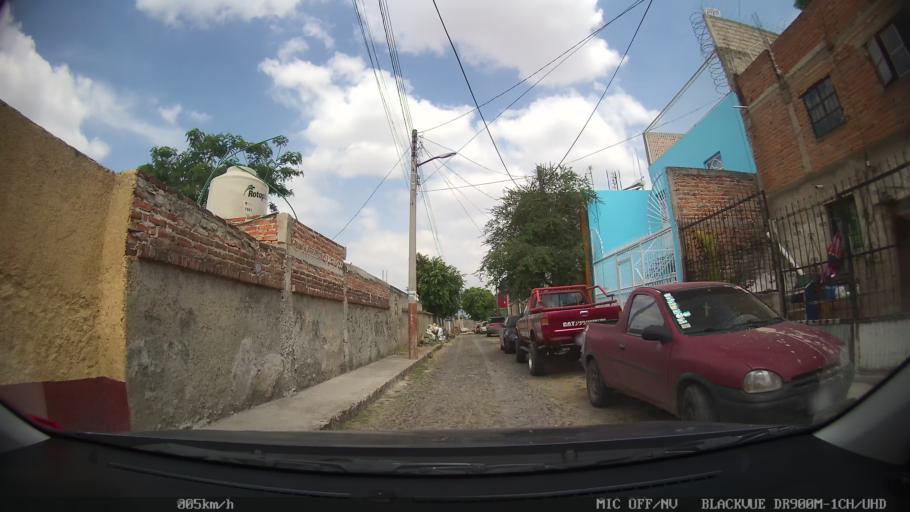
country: MX
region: Jalisco
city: Tonala
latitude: 20.6287
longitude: -103.2411
